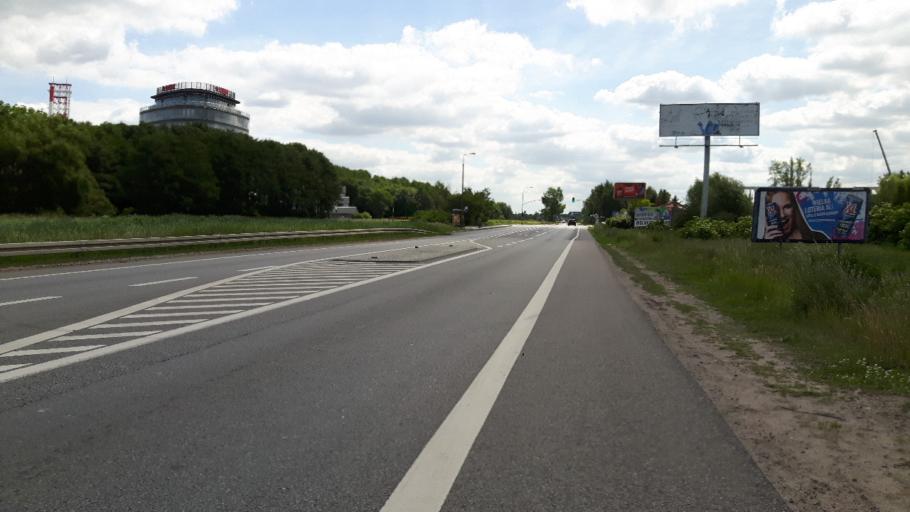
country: PL
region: Pomeranian Voivodeship
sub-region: Gdansk
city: Gdansk
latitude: 54.3445
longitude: 18.7204
